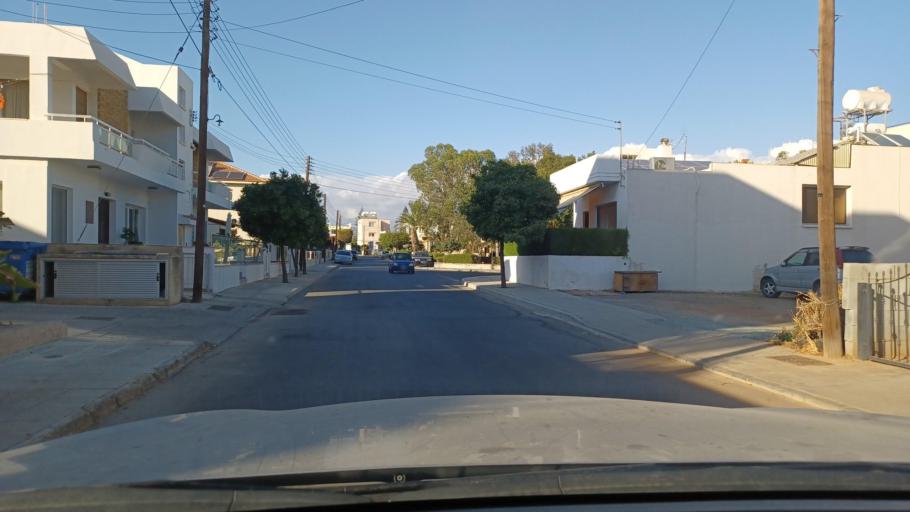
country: CY
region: Limassol
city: Limassol
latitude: 34.6634
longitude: 33.0043
